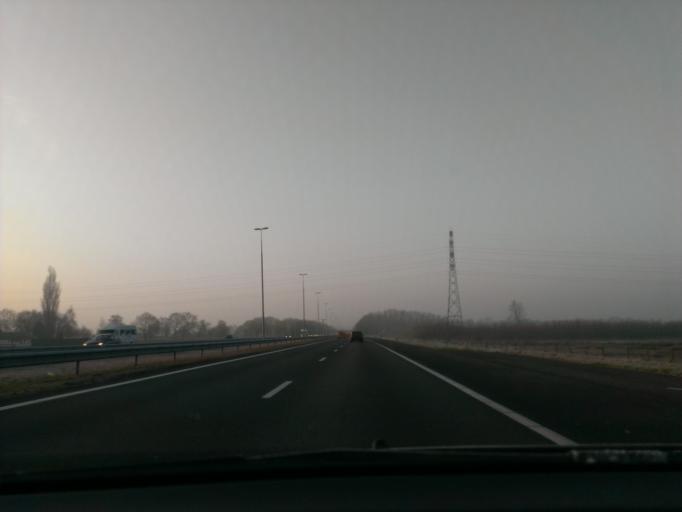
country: NL
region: Gelderland
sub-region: Gemeente Epe
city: Emst
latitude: 52.3164
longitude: 6.0060
